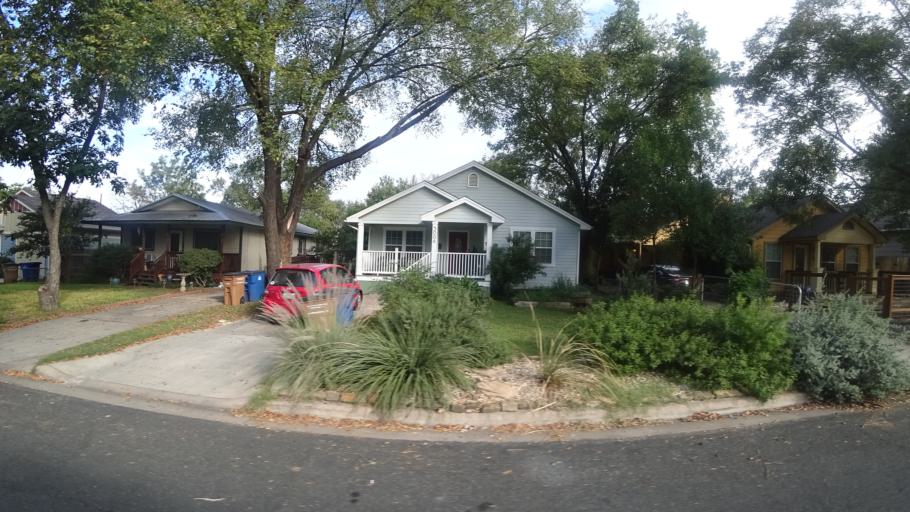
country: US
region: Texas
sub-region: Travis County
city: Austin
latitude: 30.2794
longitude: -97.7045
